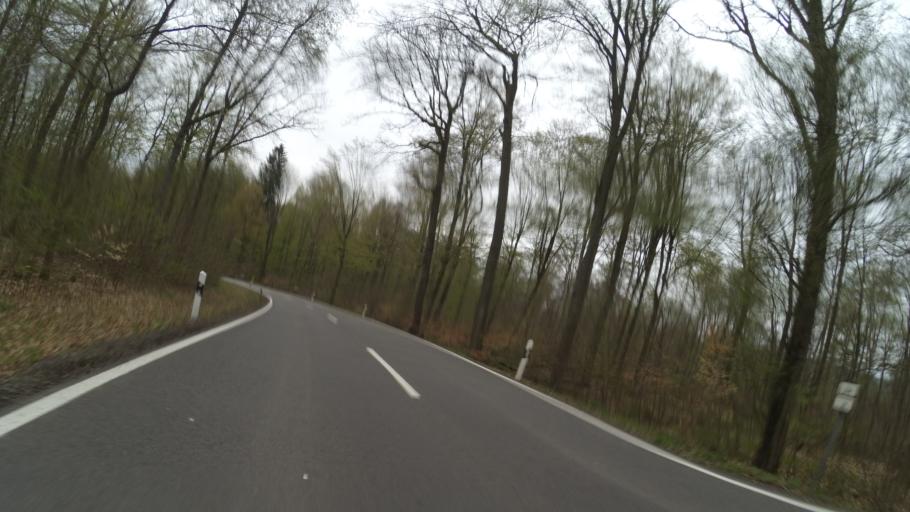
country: DE
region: Saarland
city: Friedrichsthal
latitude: 49.3022
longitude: 7.0876
